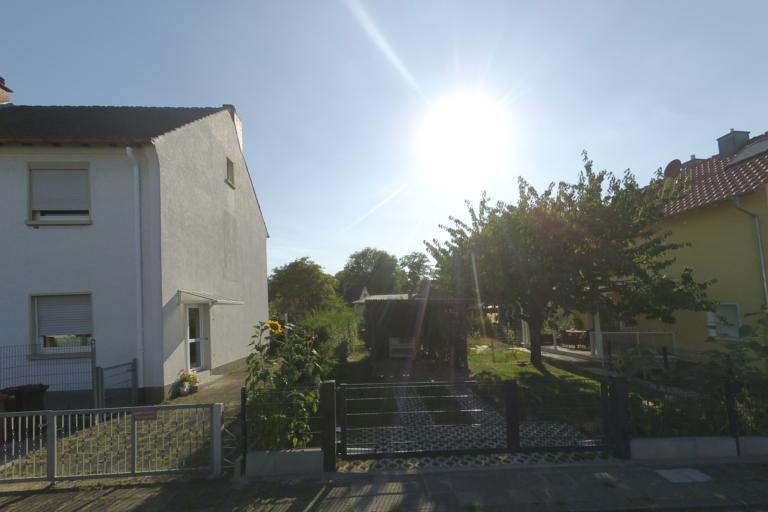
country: DE
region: Rheinland-Pfalz
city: Gartenstadt
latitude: 49.4659
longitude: 8.4019
